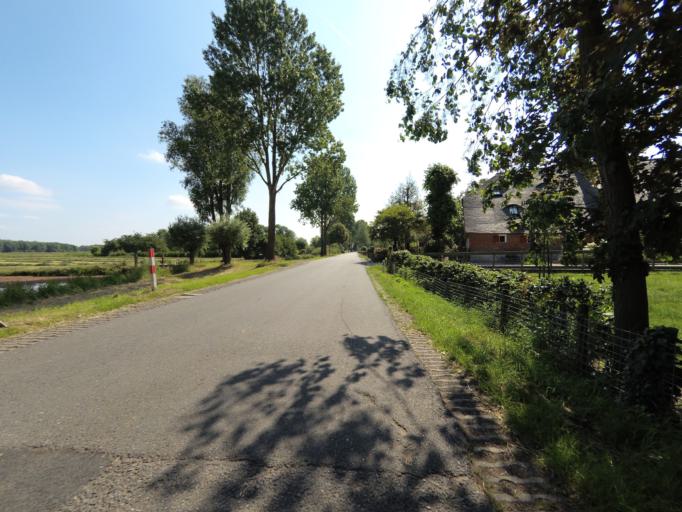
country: NL
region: Utrecht
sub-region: Gemeente Vianen
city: Vianen
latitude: 51.9490
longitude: 5.0545
